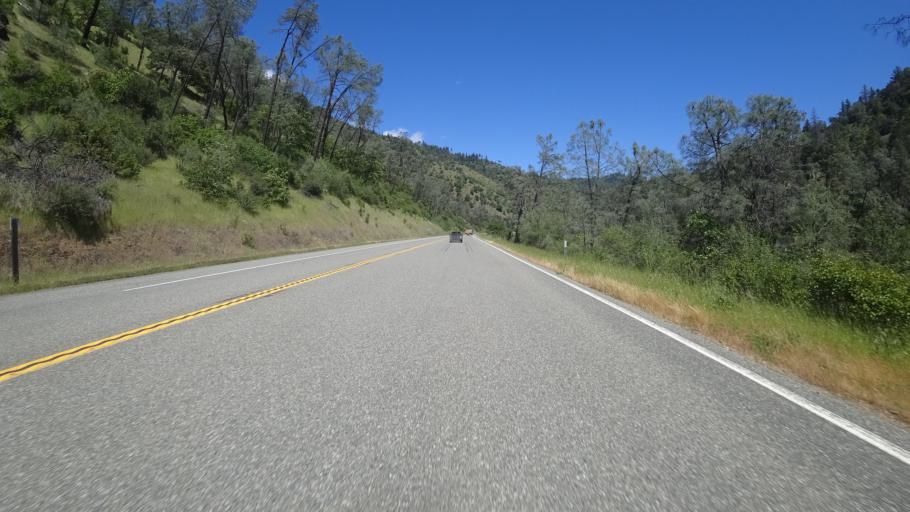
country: US
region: California
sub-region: Trinity County
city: Hayfork
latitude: 40.7369
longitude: -123.2269
